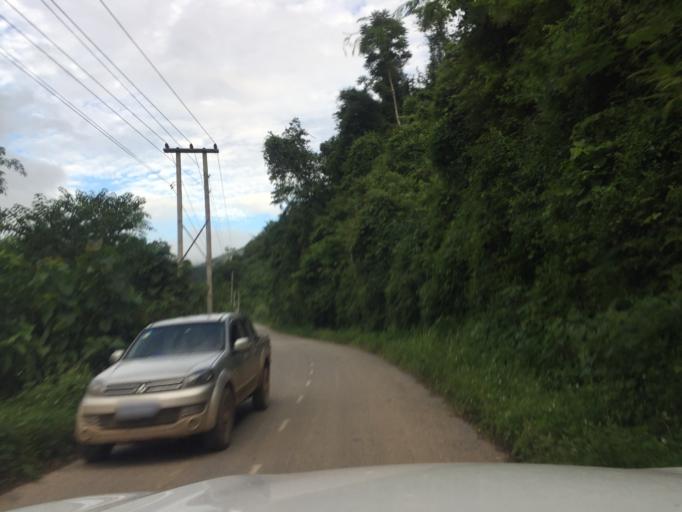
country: LA
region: Phongsali
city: Khoa
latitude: 21.1035
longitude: 102.3019
